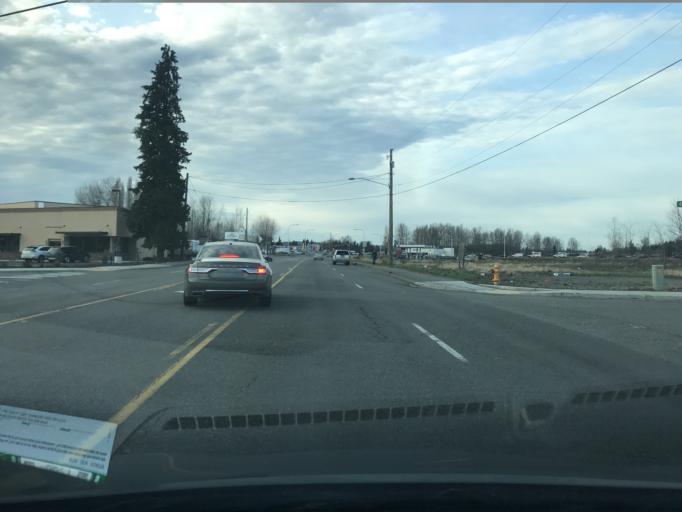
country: US
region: Washington
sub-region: King County
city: Kent
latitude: 47.3510
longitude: -122.2268
